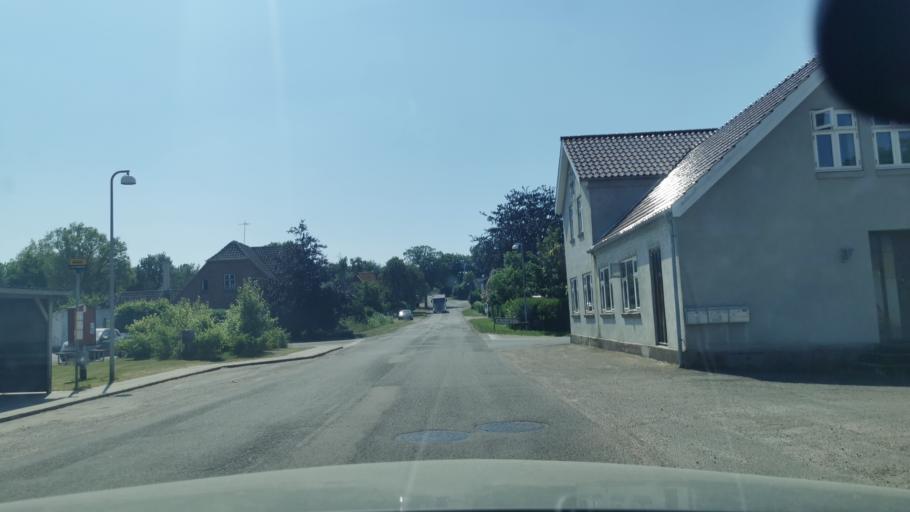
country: DK
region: Zealand
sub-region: Kalundborg Kommune
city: Hong
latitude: 55.4865
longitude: 11.2949
